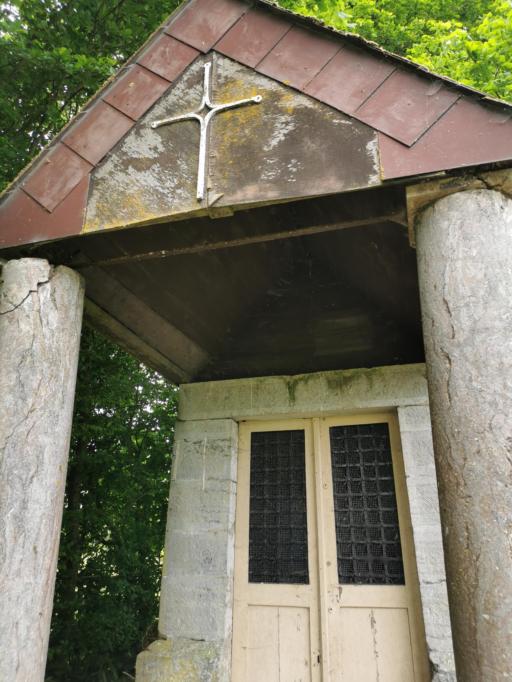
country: FR
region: Nord-Pas-de-Calais
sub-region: Departement du Nord
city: Trelon
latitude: 50.0498
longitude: 4.1134
